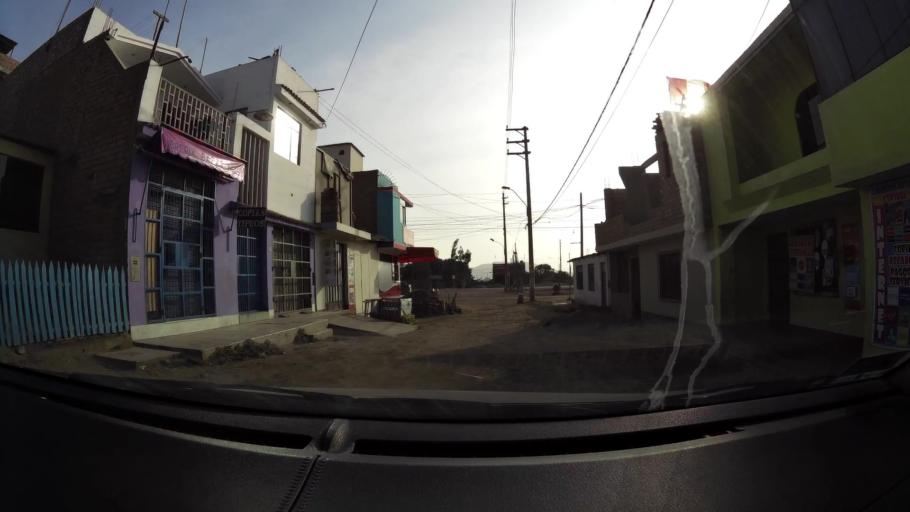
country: PE
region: Lima
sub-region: Lima
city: Santa Rosa
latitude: -11.7693
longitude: -77.1601
